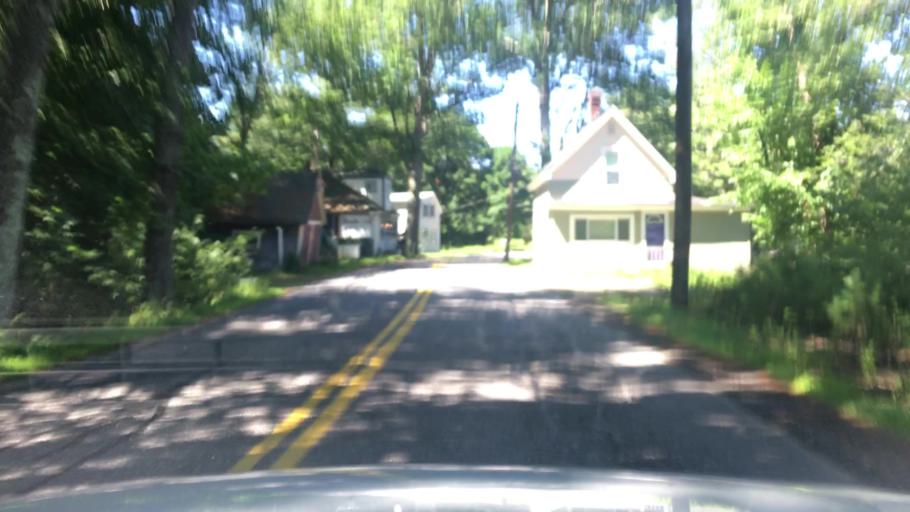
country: US
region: New Hampshire
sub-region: Merrimack County
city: Boscawen
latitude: 43.2624
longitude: -71.6189
